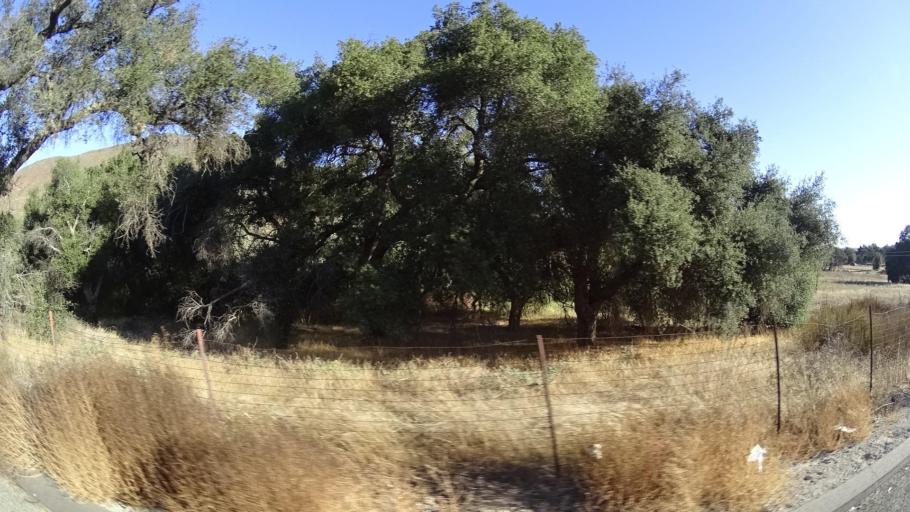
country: MX
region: Baja California
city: Tecate
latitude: 32.6087
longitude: -116.6276
